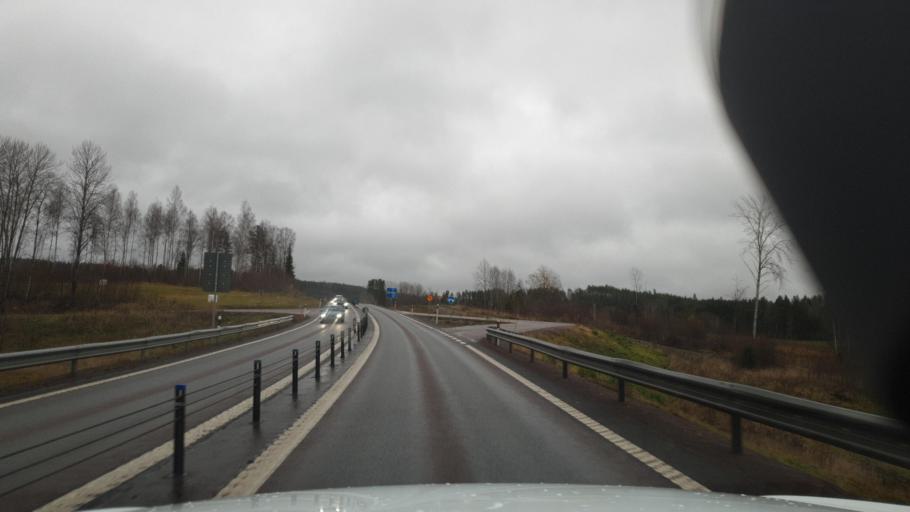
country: SE
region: Vaermland
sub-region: Arvika Kommun
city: Arvika
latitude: 59.6610
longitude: 12.7850
